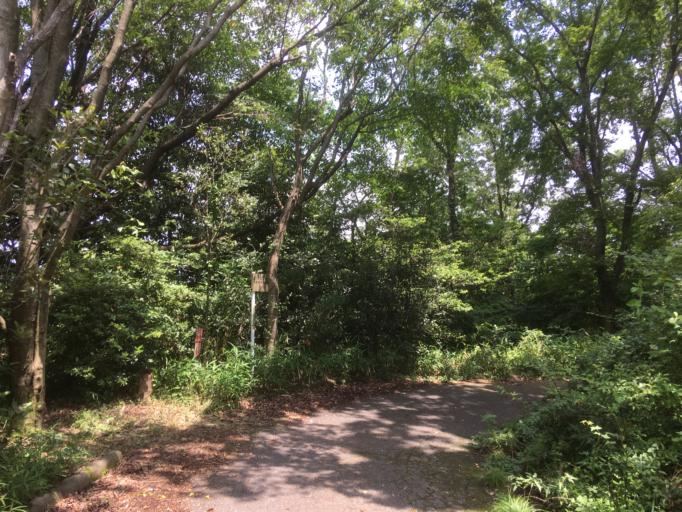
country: JP
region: Nara
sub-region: Ikoma-shi
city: Ikoma
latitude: 34.6922
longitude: 135.6698
